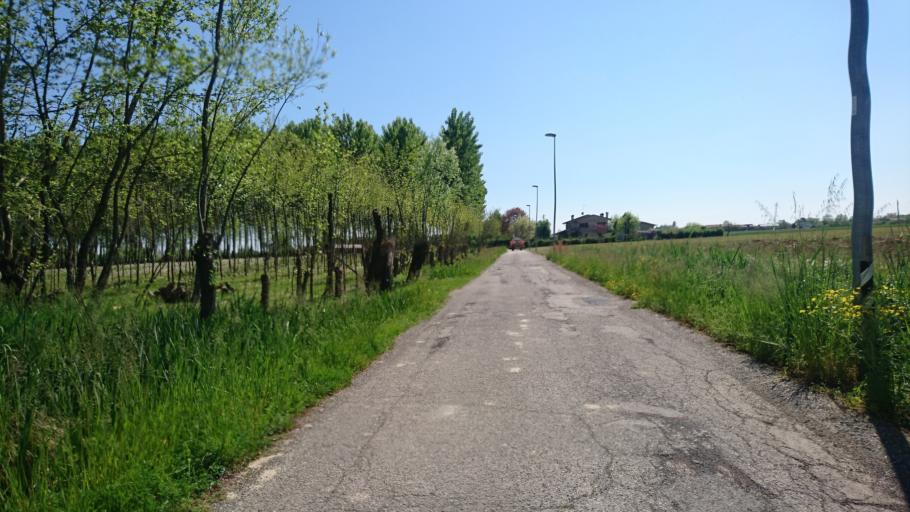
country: IT
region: Veneto
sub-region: Provincia di Treviso
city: Conscio
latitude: 45.6234
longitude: 12.2751
